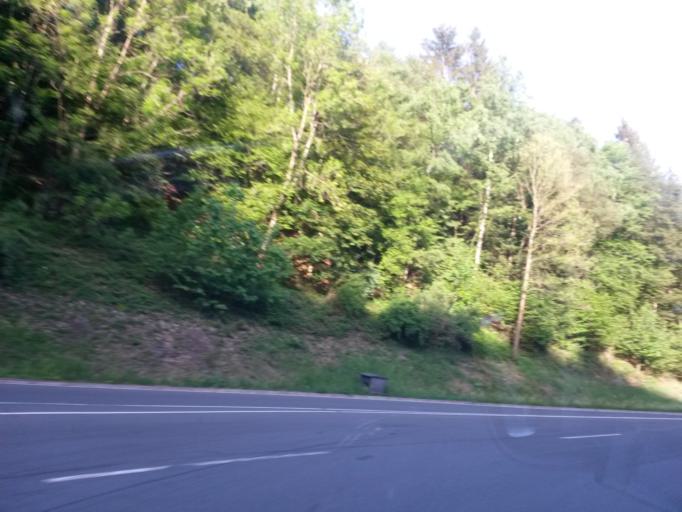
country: DE
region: North Rhine-Westphalia
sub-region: Regierungsbezirk Arnsberg
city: Drolshagen
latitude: 51.0483
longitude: 7.7343
